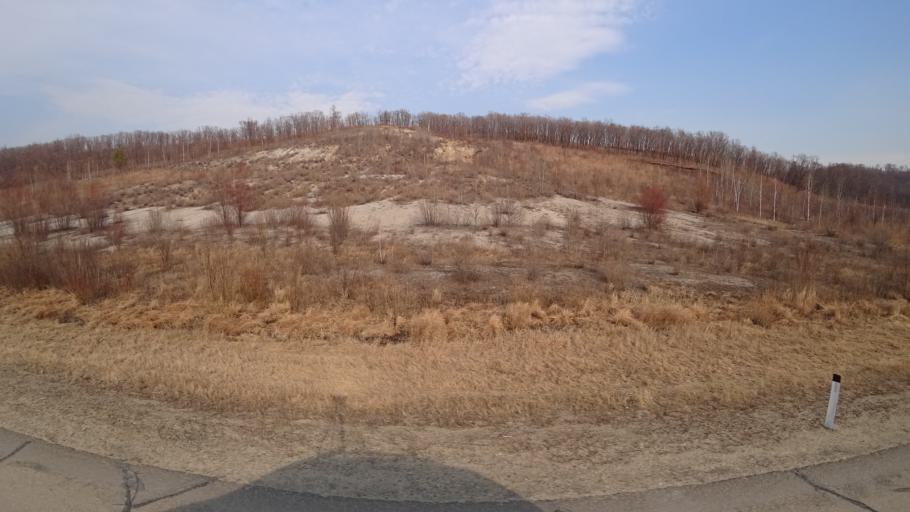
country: RU
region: Amur
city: Novobureyskiy
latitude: 49.8748
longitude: 129.8850
